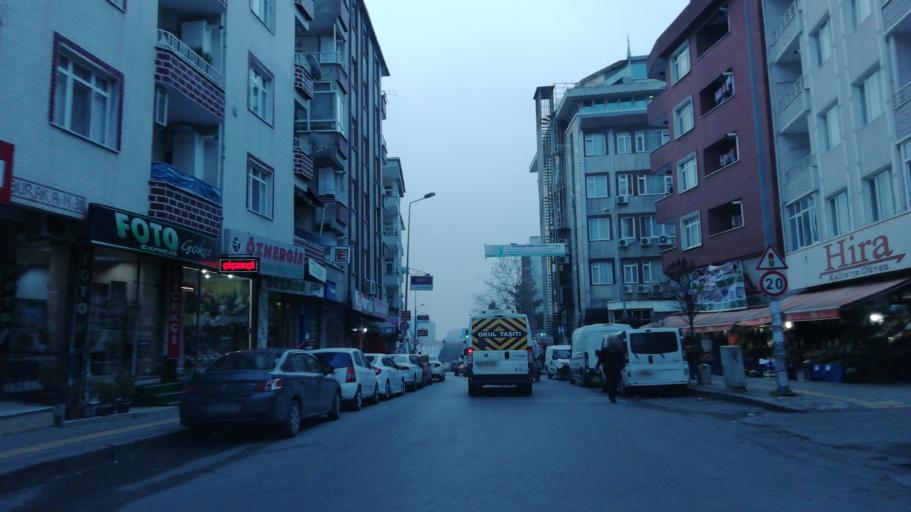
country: TR
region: Istanbul
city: Bahcelievler
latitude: 40.9999
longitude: 28.8303
